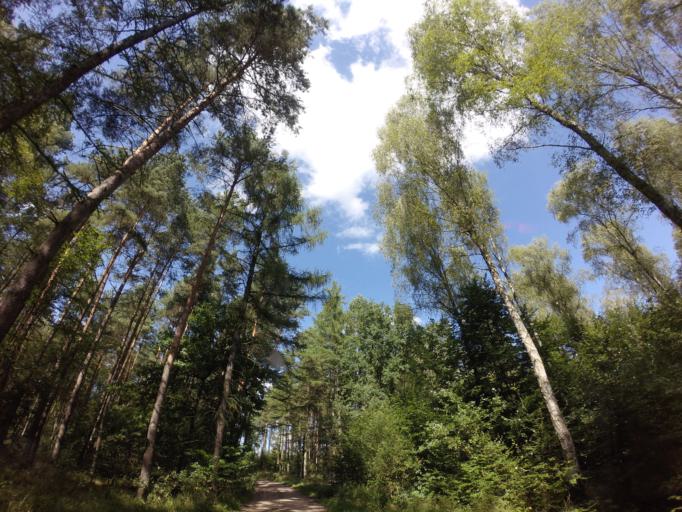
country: PL
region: West Pomeranian Voivodeship
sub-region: Powiat choszczenski
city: Drawno
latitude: 53.2360
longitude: 15.6717
